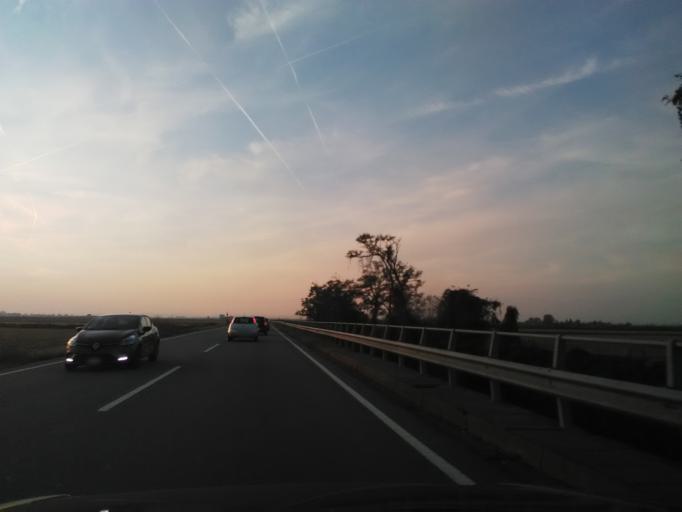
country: IT
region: Piedmont
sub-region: Provincia di Vercelli
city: Olcenengo
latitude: 45.3346
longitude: 8.3074
